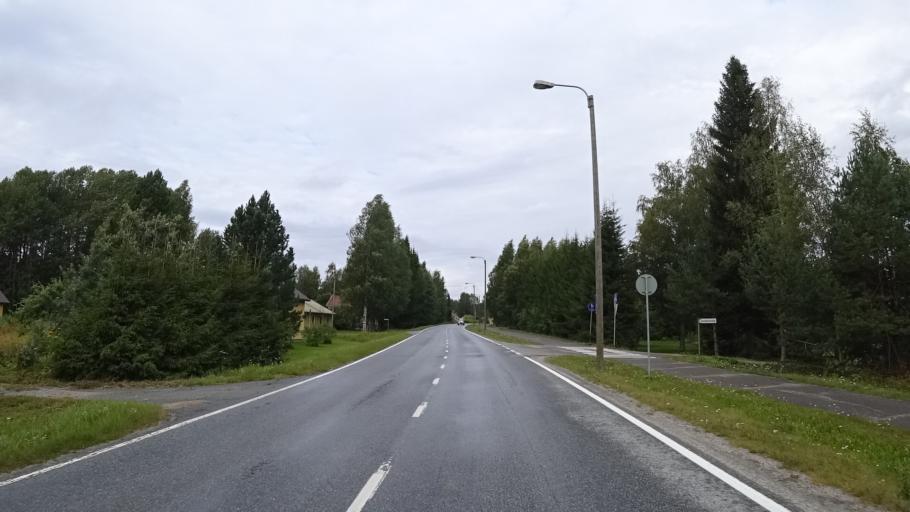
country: FI
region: Southern Savonia
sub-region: Savonlinna
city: Kerimaeki
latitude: 61.9223
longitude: 29.2805
